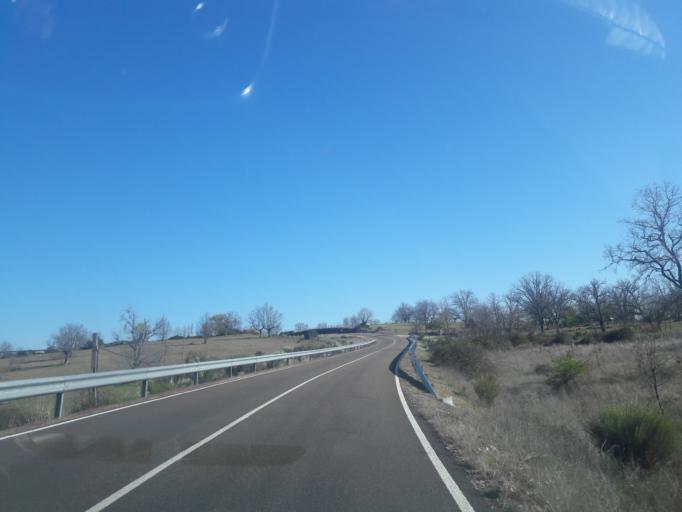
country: ES
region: Castille and Leon
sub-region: Provincia de Salamanca
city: Cabeza del Caballo
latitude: 41.1046
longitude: -6.5549
